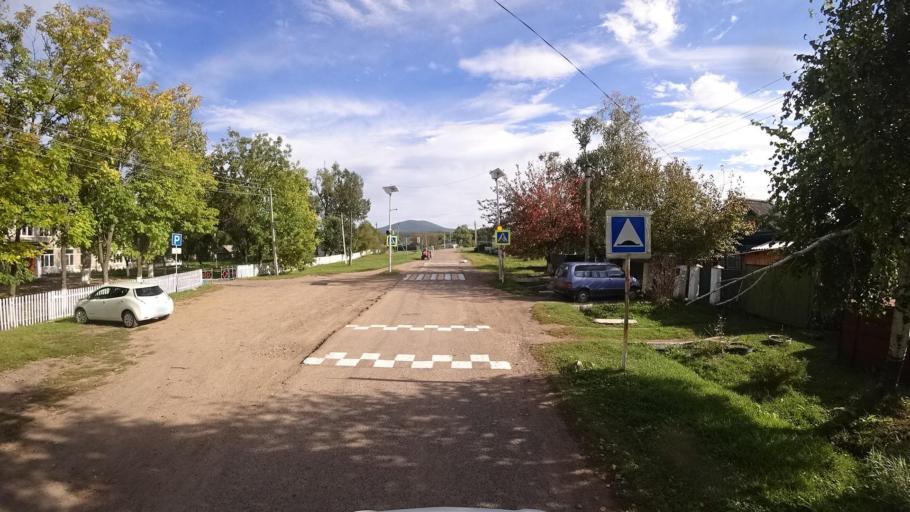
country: RU
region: Primorskiy
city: Dostoyevka
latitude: 44.2968
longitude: 133.4537
